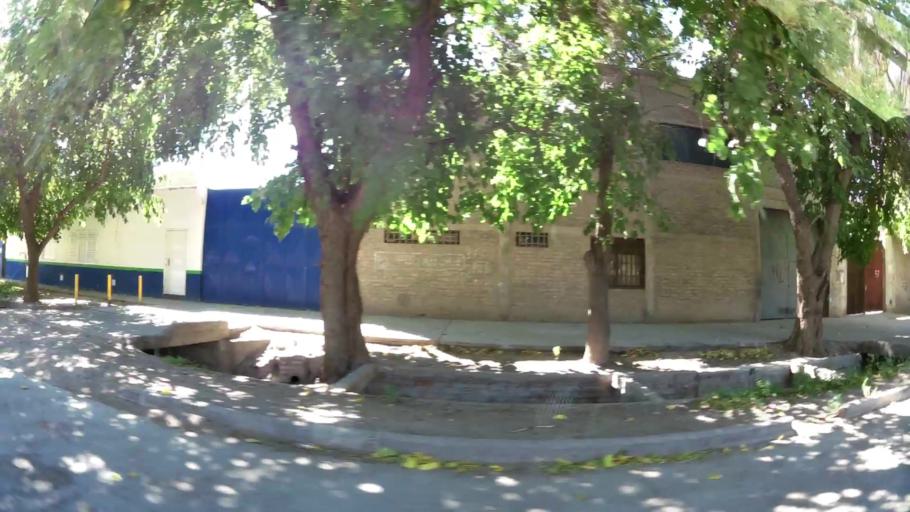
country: AR
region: Mendoza
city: Las Heras
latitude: -32.8316
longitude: -68.8341
